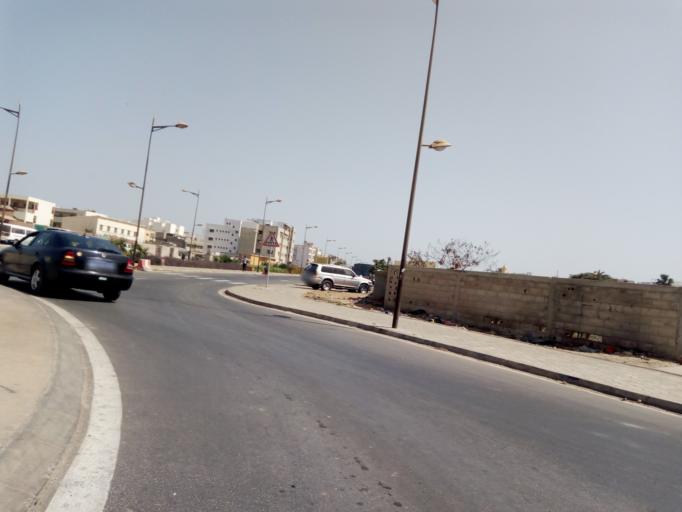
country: SN
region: Dakar
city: Dakar
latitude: 14.7017
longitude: -17.4507
